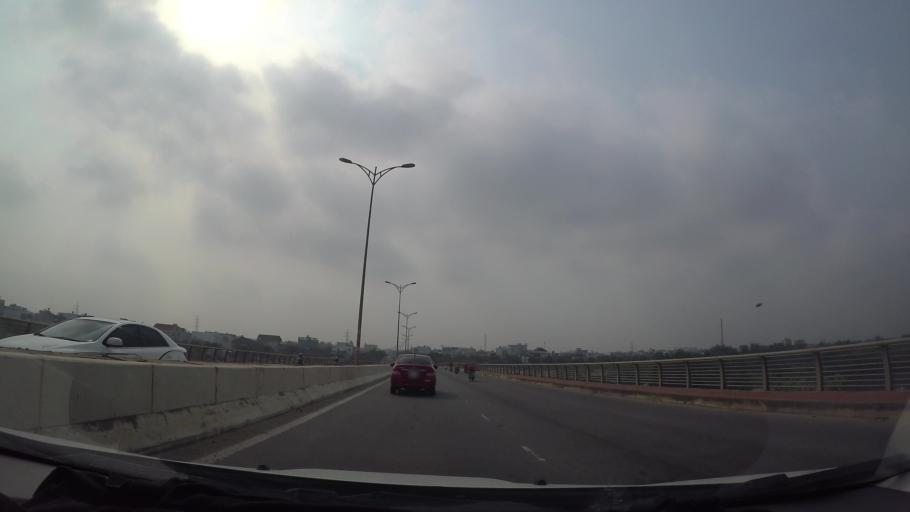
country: VN
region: Da Nang
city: Cam Le
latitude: 16.0135
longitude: 108.2152
